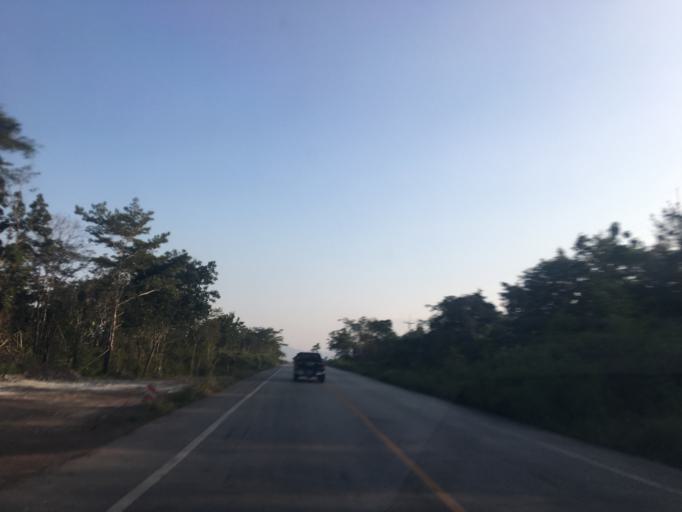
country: TH
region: Lampang
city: Ngao
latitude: 18.6957
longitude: 100.0019
